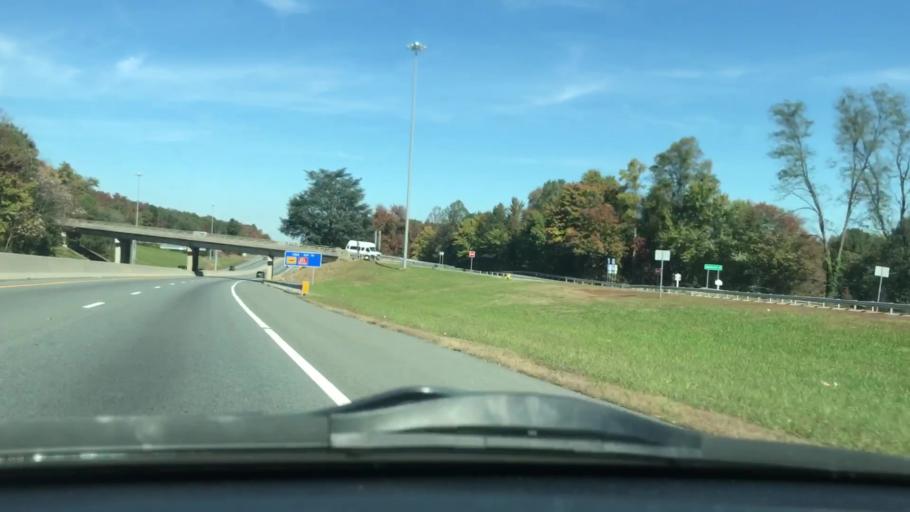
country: US
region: North Carolina
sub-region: Randolph County
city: Asheboro
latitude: 35.7185
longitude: -79.8264
